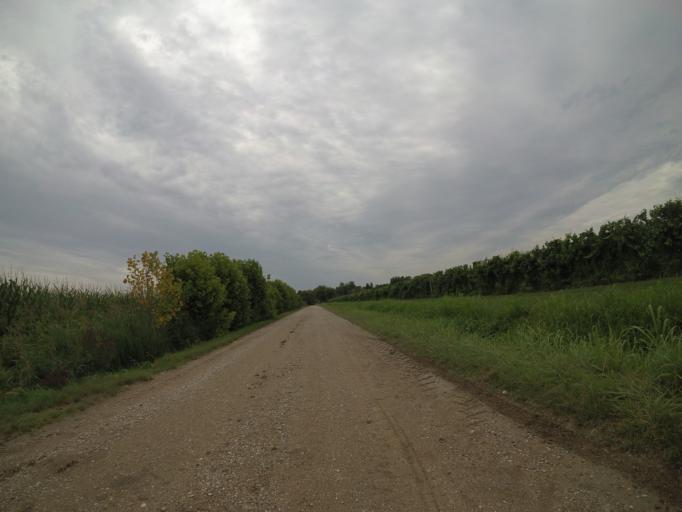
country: IT
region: Friuli Venezia Giulia
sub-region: Provincia di Udine
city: Rivignano
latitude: 45.9048
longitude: 13.0583
